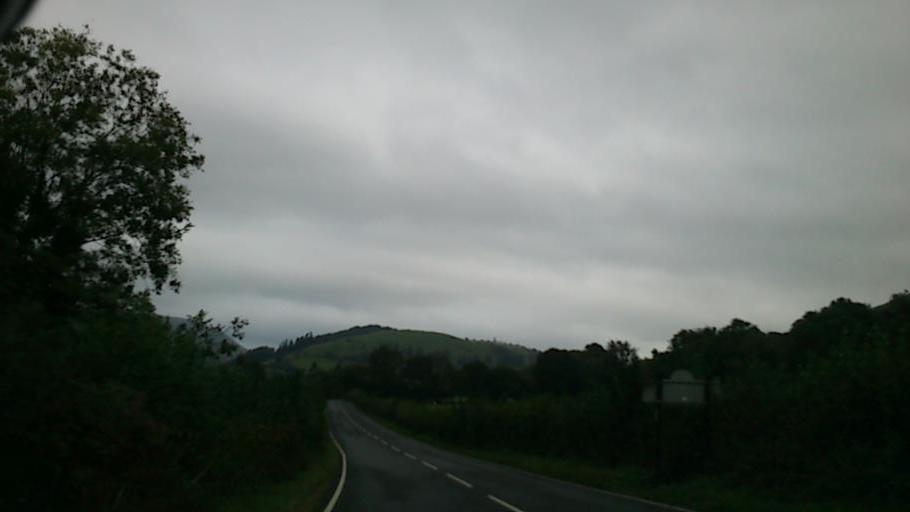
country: GB
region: Wales
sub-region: Gwynedd
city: Corris
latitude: 52.6913
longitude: -3.6839
